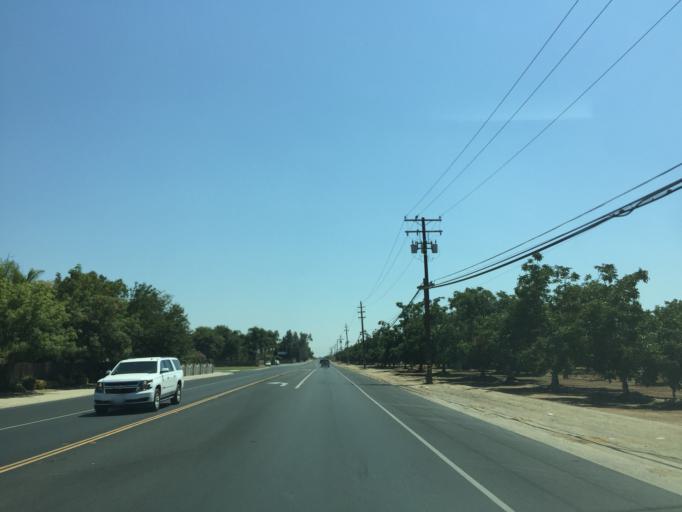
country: US
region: California
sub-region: Tulare County
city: Visalia
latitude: 36.3701
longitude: -119.2970
